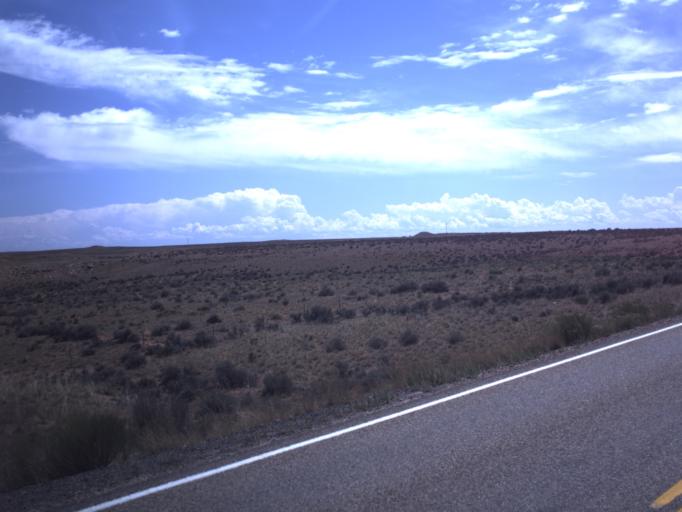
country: US
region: Utah
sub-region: Uintah County
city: Maeser
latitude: 40.3108
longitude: -109.6911
